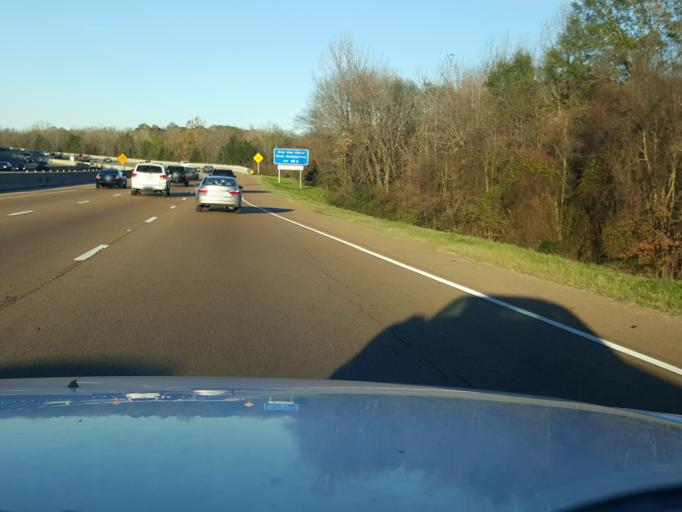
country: US
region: Mississippi
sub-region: Rankin County
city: Flowood
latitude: 32.3138
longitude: -90.1598
